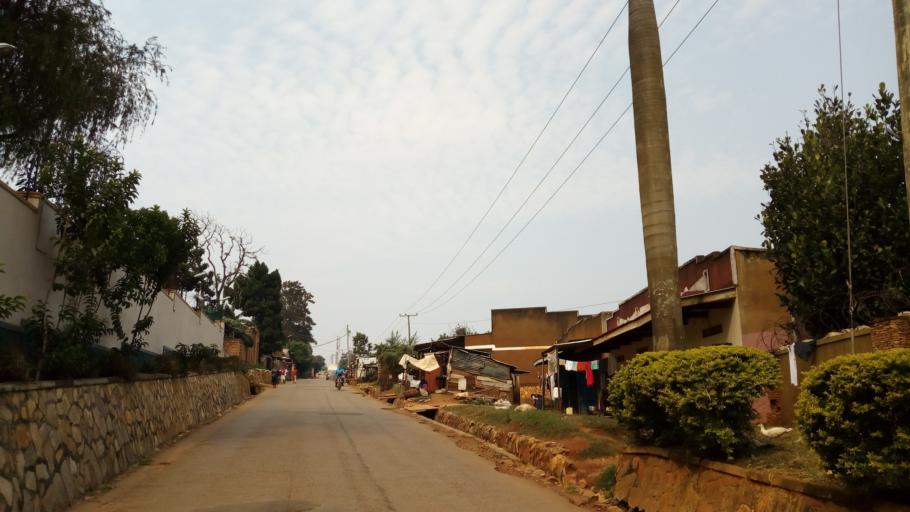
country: UG
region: Central Region
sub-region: Wakiso District
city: Kireka
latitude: 0.3096
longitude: 32.6428
